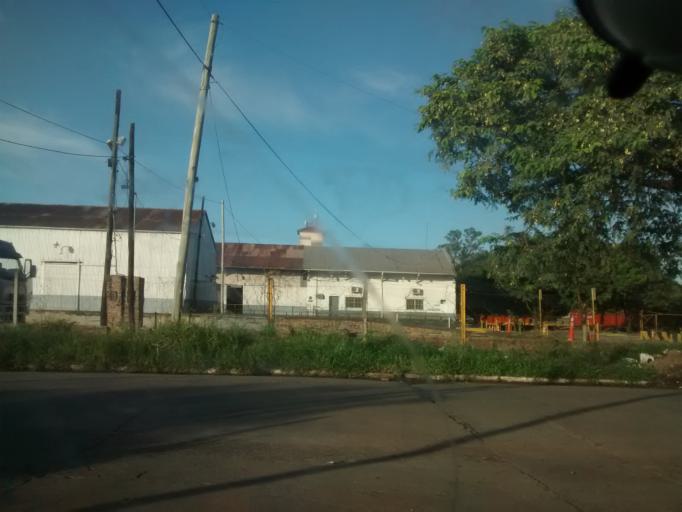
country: AR
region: Chaco
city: Resistencia
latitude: -27.4640
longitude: -58.9796
